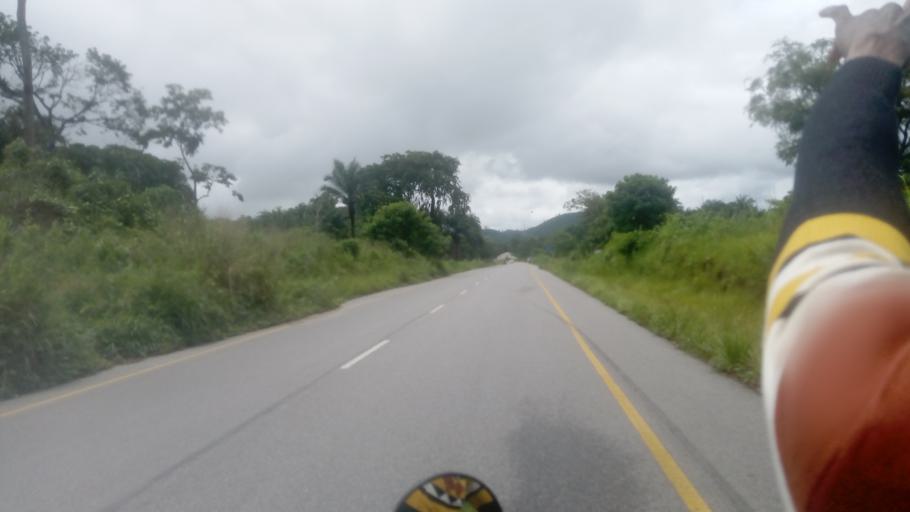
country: SL
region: Northern Province
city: Makali
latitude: 8.6318
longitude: -11.6671
